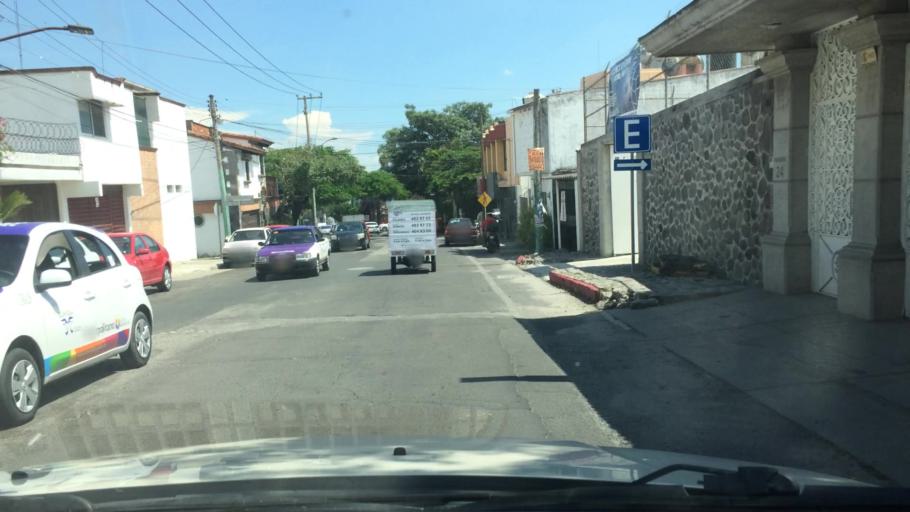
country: MX
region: Morelos
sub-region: Cuernavaca
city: Cuernavaca
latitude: 18.9081
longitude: -99.2279
